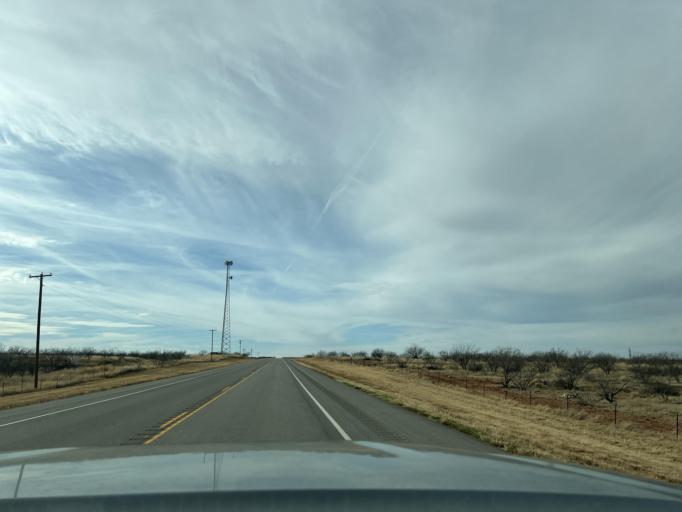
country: US
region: Texas
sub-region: Jones County
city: Anson
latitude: 32.7508
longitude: -99.7219
